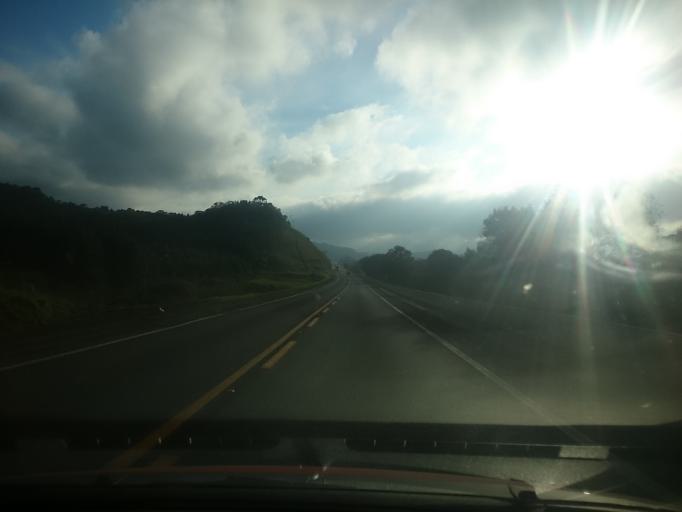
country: BR
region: Santa Catarina
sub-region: Lages
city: Lages
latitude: -27.9947
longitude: -50.5282
